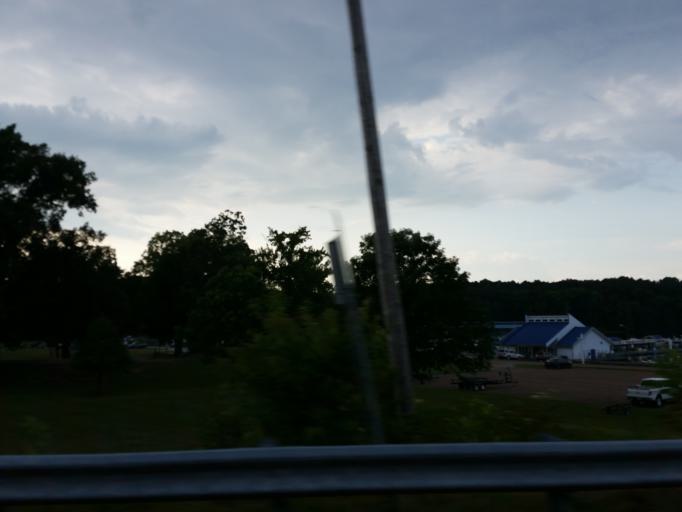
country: US
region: Tennessee
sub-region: Stewart County
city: Dover
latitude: 36.4394
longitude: -88.0819
